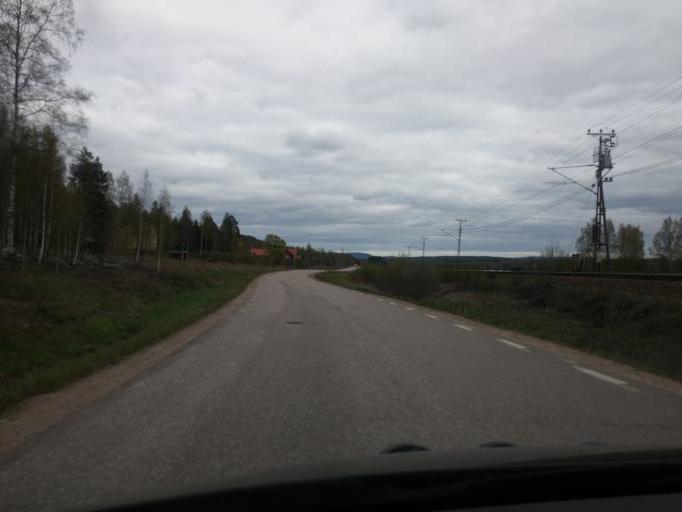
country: SE
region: Gaevleborg
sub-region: Ljusdals Kommun
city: Ljusdal
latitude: 61.8494
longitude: 16.0489
